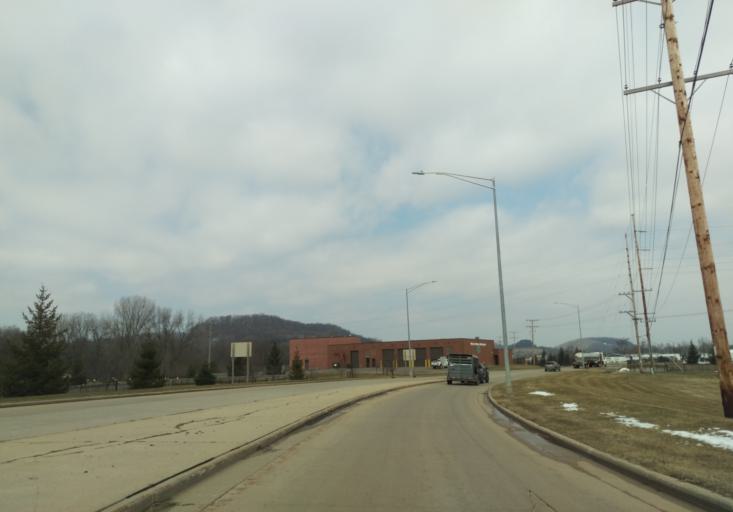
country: US
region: Wisconsin
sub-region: Richland County
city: Richland Center
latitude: 43.3301
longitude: -90.3875
